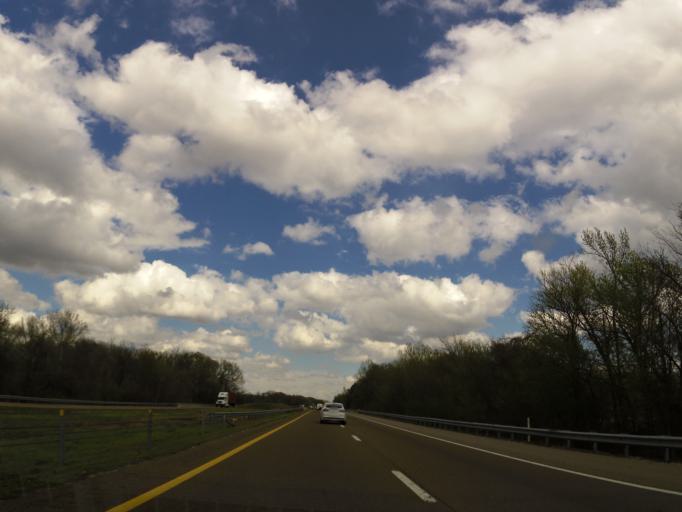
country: US
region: Tennessee
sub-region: Crockett County
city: Bells
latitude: 35.6074
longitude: -89.0280
